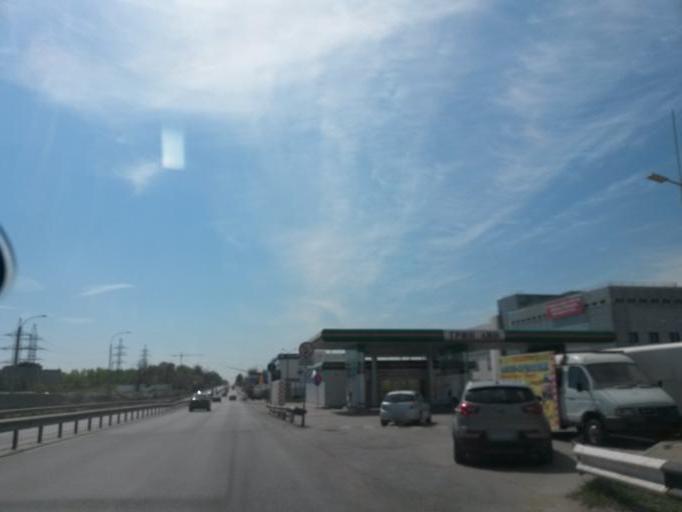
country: RU
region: Moskovskaya
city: Shcherbinka
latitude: 55.4928
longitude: 37.5689
